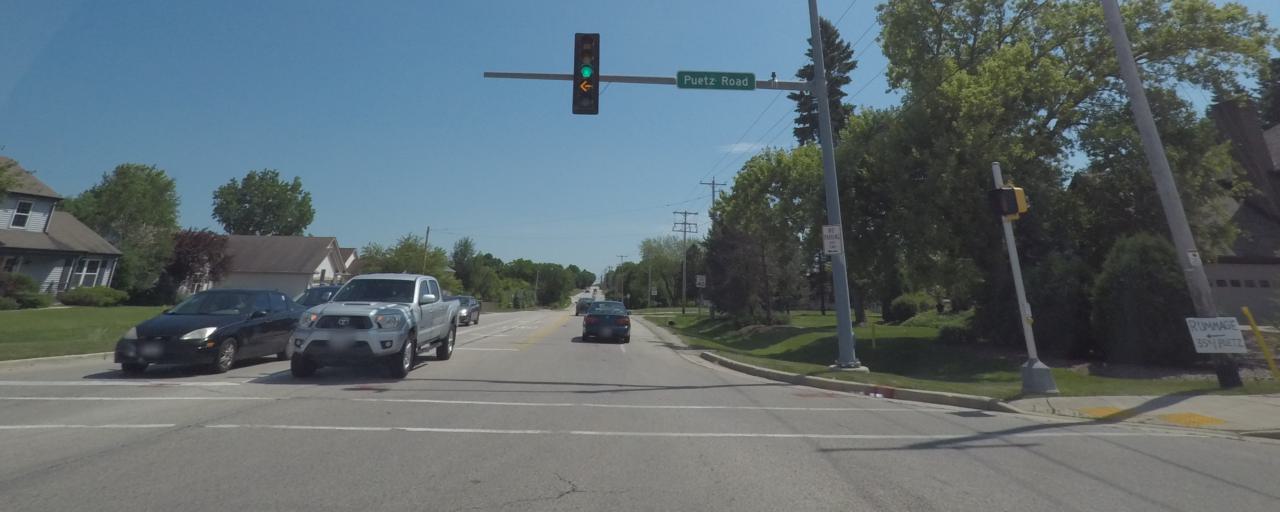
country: US
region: Wisconsin
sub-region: Milwaukee County
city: Oak Creek
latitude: 42.8871
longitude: -87.9318
